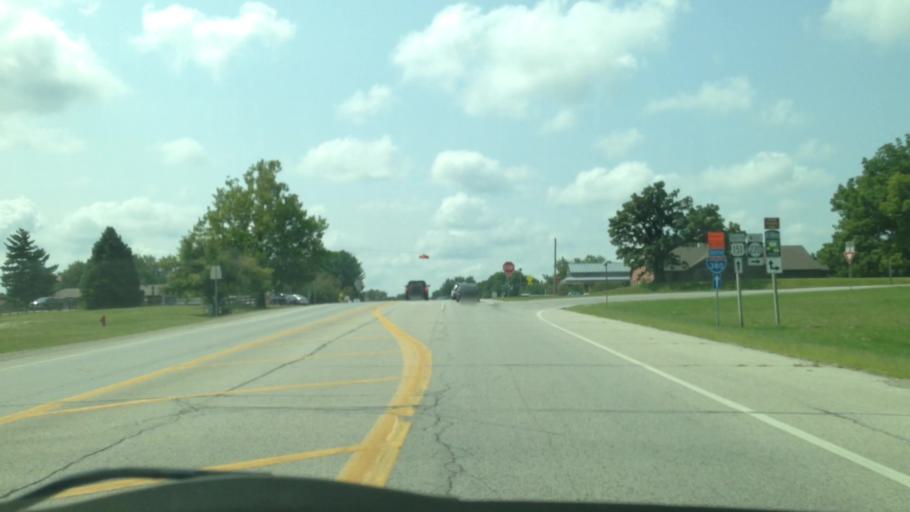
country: US
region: Iowa
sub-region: Benton County
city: Walford
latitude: 41.8027
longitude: -91.8741
